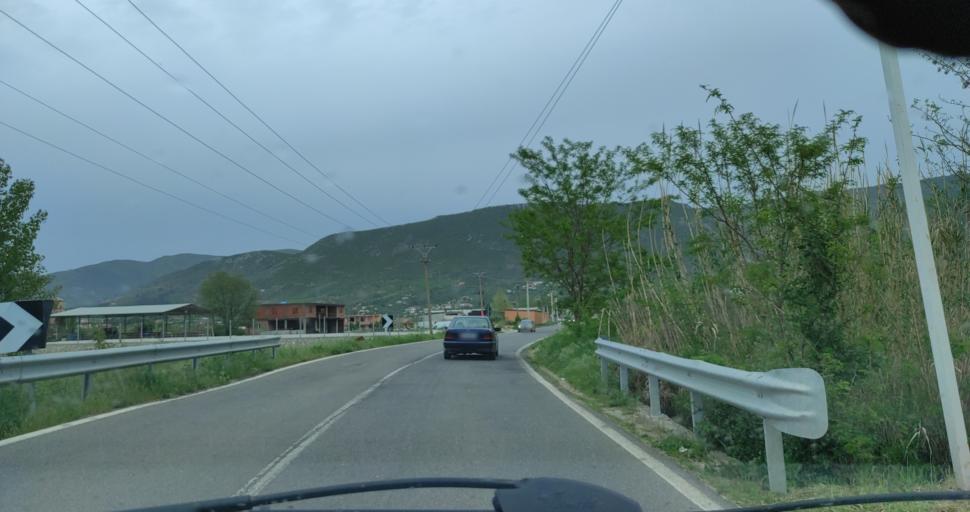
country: AL
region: Lezhe
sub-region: Rrethi i Kurbinit
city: Lac
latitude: 41.6046
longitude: 19.7082
